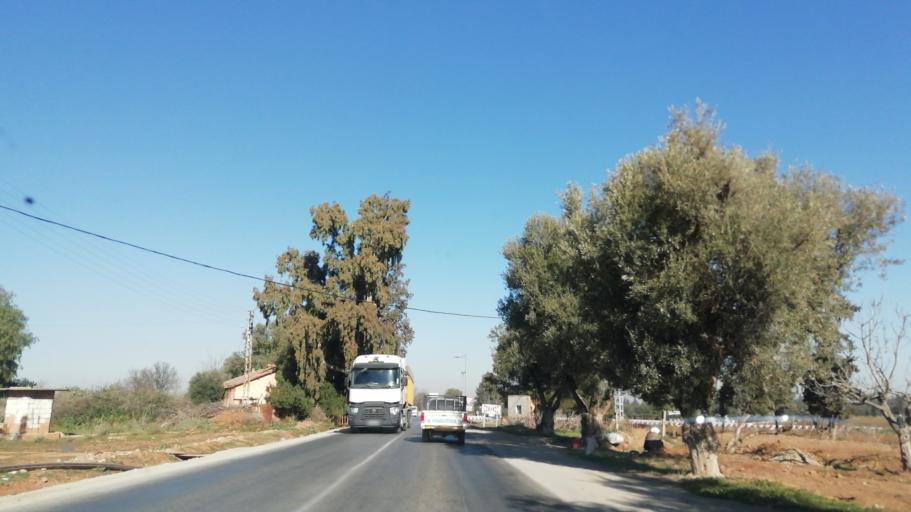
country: DZ
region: Mascara
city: Mascara
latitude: 35.2746
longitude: 0.1285
